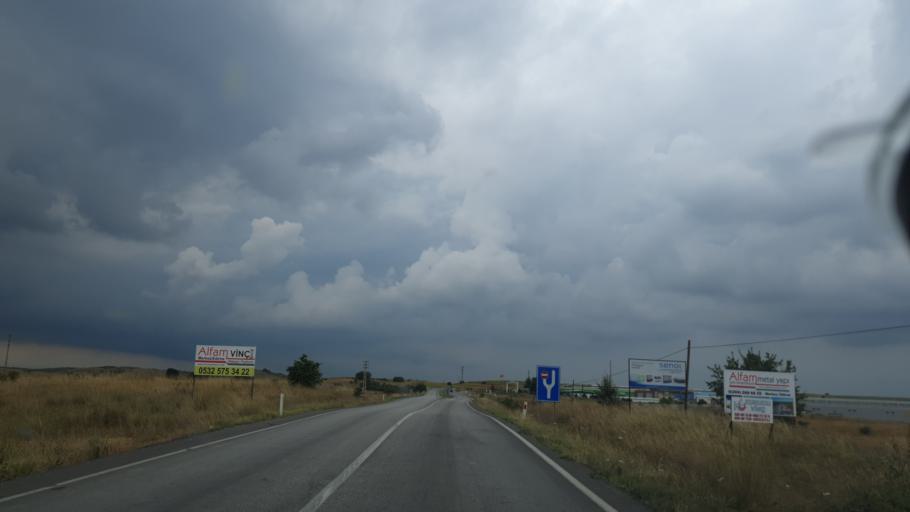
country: TR
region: Tekirdag
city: Hayrabolu
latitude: 41.2202
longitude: 27.0511
